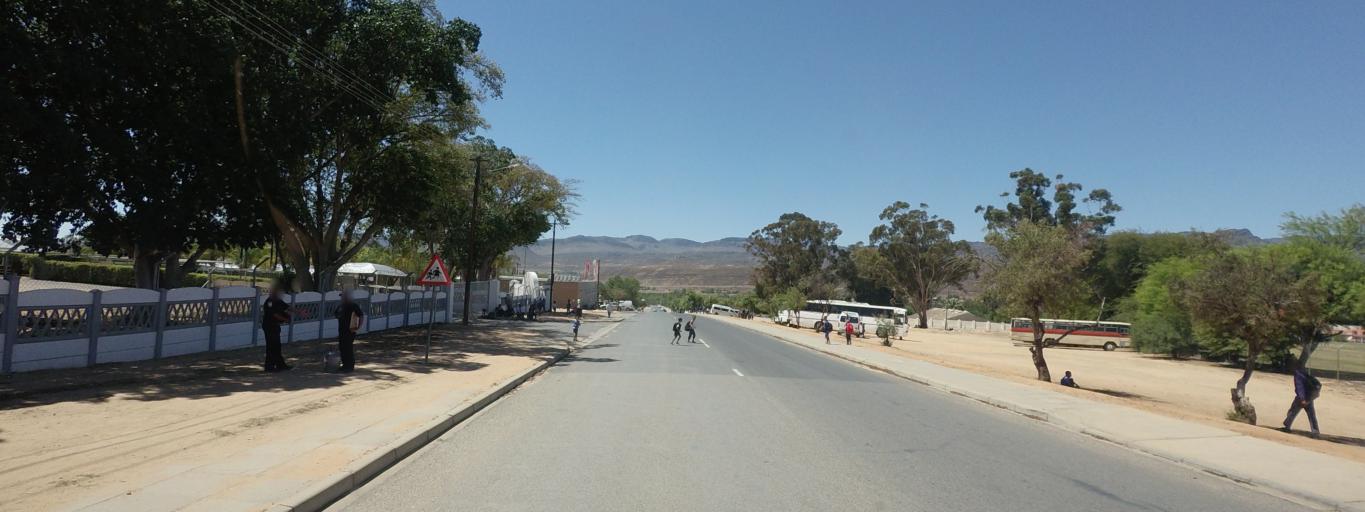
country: ZA
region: Western Cape
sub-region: West Coast District Municipality
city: Clanwilliam
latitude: -32.1879
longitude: 18.8898
